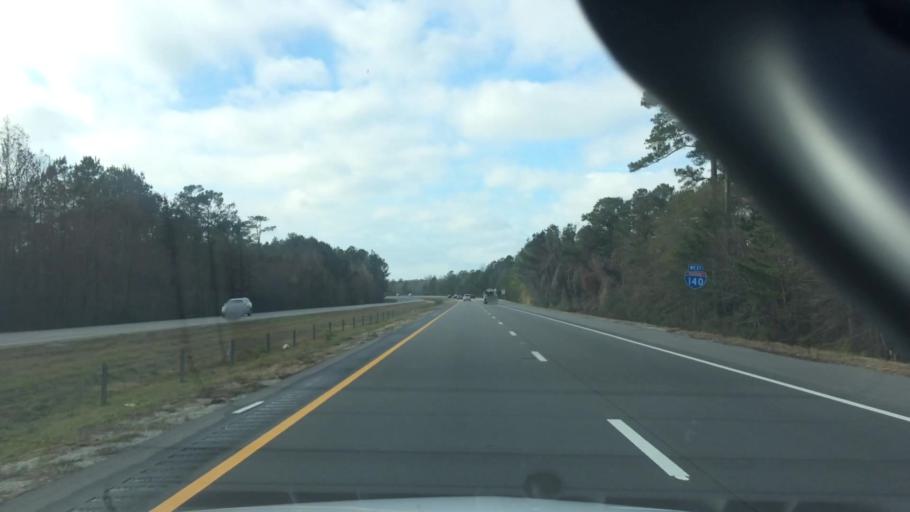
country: US
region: North Carolina
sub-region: New Hanover County
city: Wrightsboro
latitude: 34.3184
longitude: -77.9277
